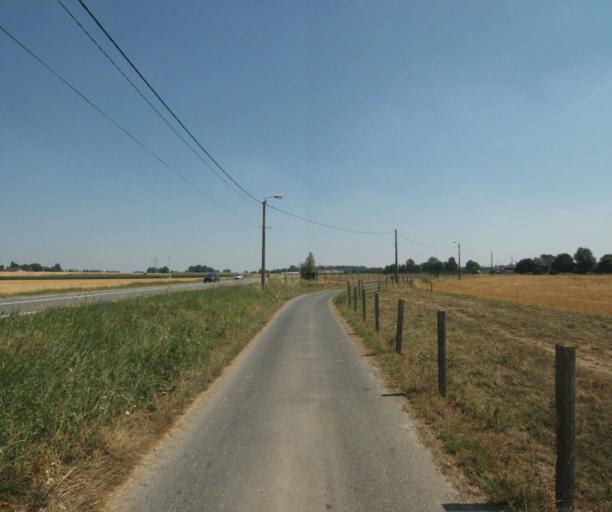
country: FR
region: Nord-Pas-de-Calais
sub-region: Departement du Nord
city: Wervicq-Sud
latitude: 50.7507
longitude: 3.0392
